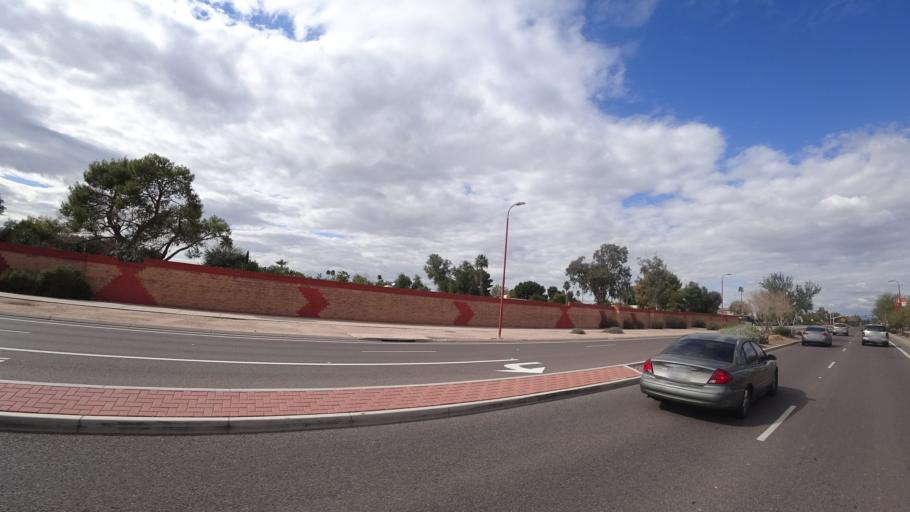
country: US
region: Arizona
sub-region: Maricopa County
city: Scottsdale
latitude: 33.5427
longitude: -111.8913
